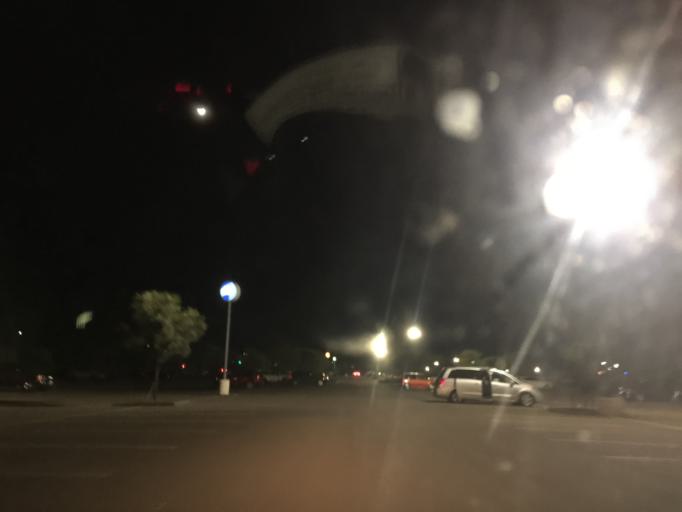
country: US
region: California
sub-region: San Diego County
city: San Diego
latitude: 32.7620
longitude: -117.2210
